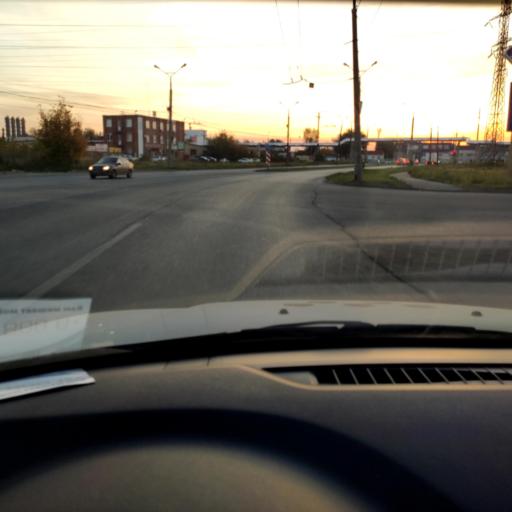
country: RU
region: Samara
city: Tol'yatti
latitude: 53.5342
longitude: 49.4366
